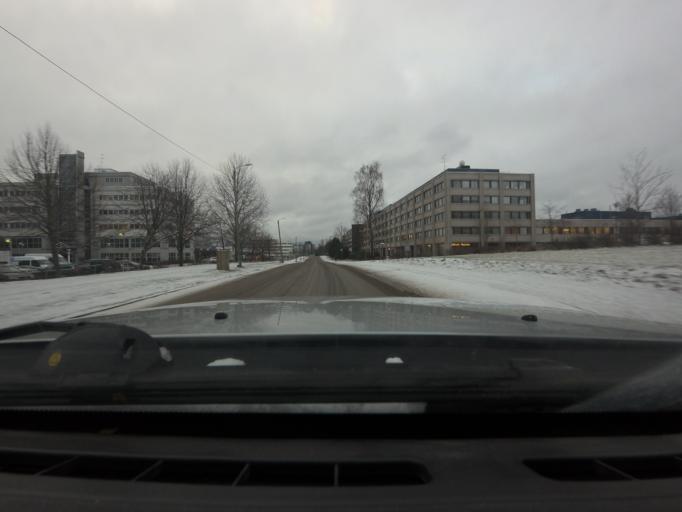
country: FI
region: Uusimaa
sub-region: Helsinki
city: Kauniainen
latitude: 60.2121
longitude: 24.7517
